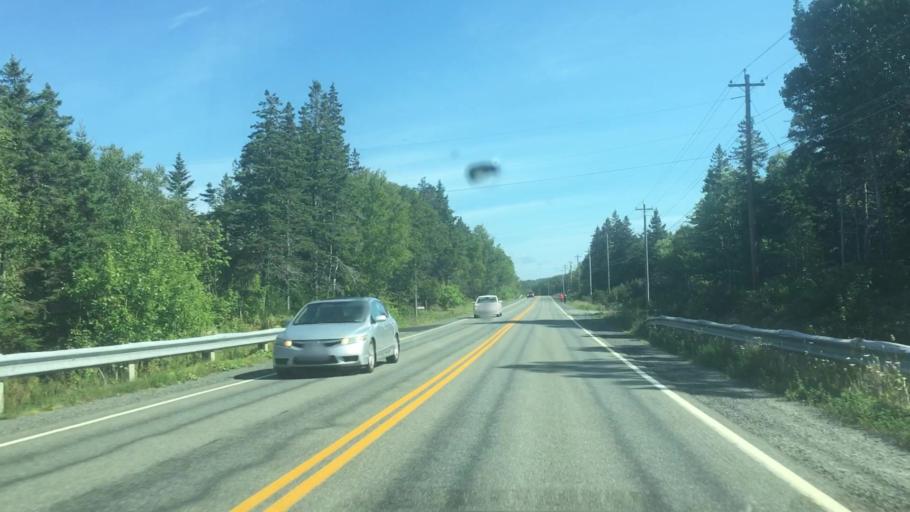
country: CA
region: Nova Scotia
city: Sydney
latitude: 45.9863
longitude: -60.4187
